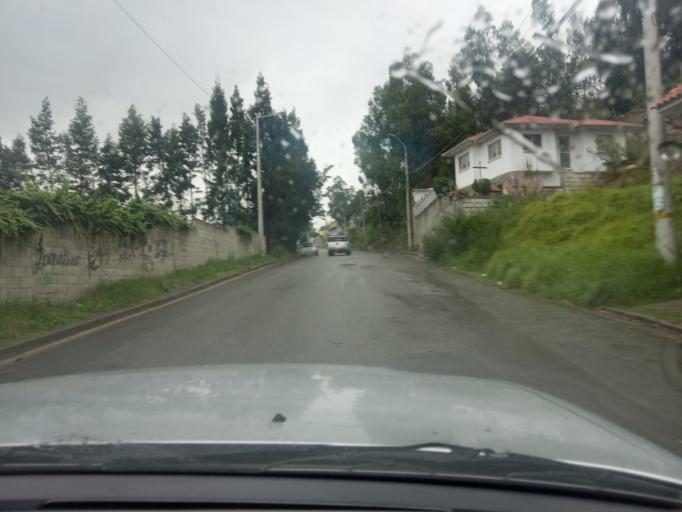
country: EC
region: Azuay
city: Llacao
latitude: -2.8625
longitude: -78.9387
